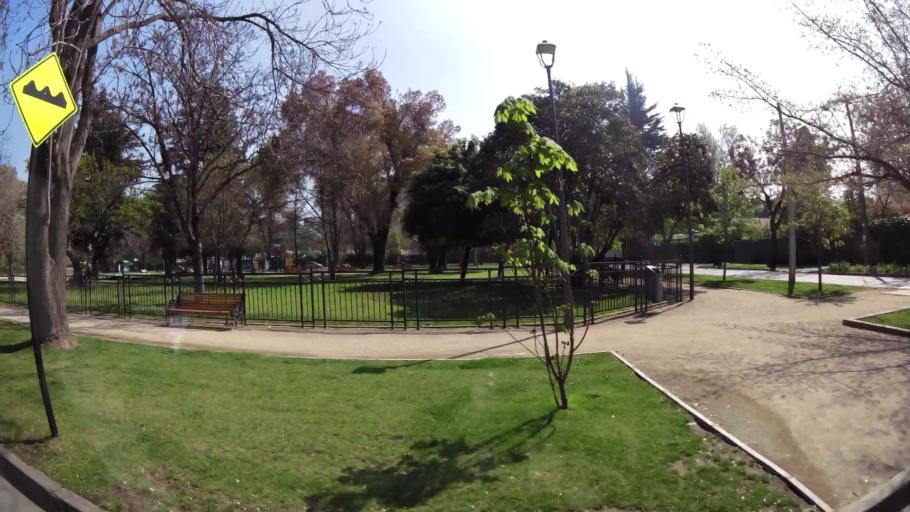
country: CL
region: Santiago Metropolitan
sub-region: Provincia de Santiago
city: Villa Presidente Frei, Nunoa, Santiago, Chile
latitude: -33.3953
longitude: -70.5948
